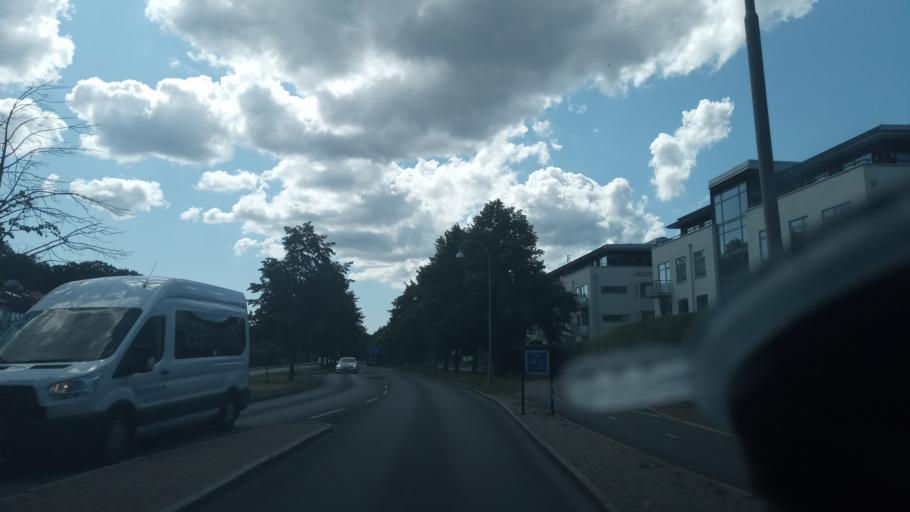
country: SE
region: Vaestra Goetaland
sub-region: Goteborg
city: Goeteborg
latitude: 57.6934
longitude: 12.0033
